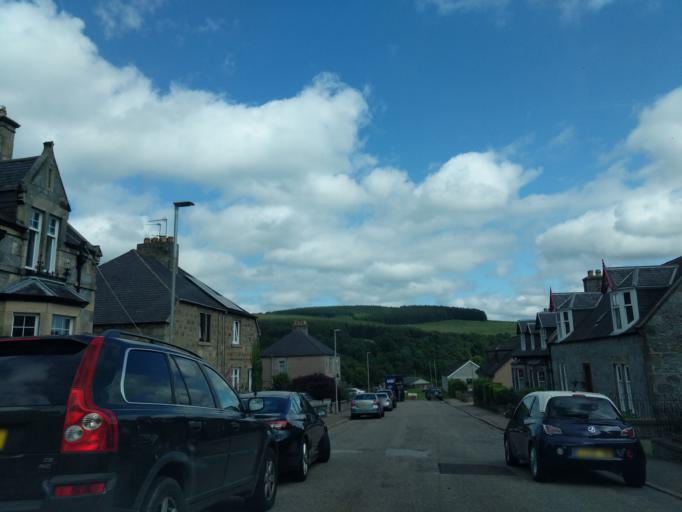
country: GB
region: Scotland
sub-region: Moray
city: Dufftown
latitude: 57.4463
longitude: -3.1242
